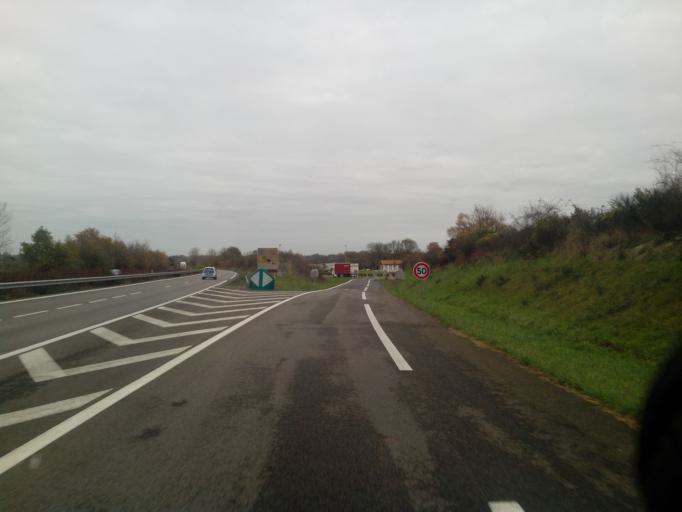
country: FR
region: Pays de la Loire
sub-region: Departement de la Loire-Atlantique
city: Le Pallet
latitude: 47.1558
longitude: -1.3165
